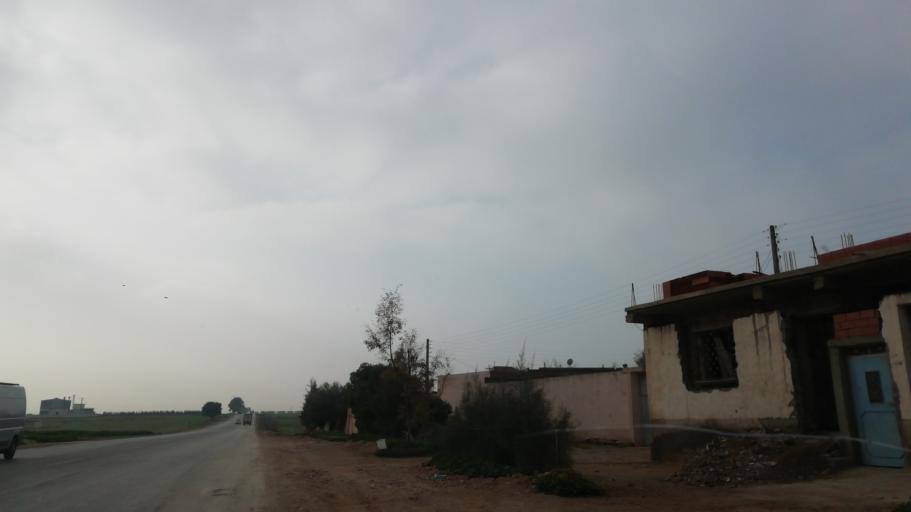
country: DZ
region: Relizane
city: Djidiouia
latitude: 35.8829
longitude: 0.7326
